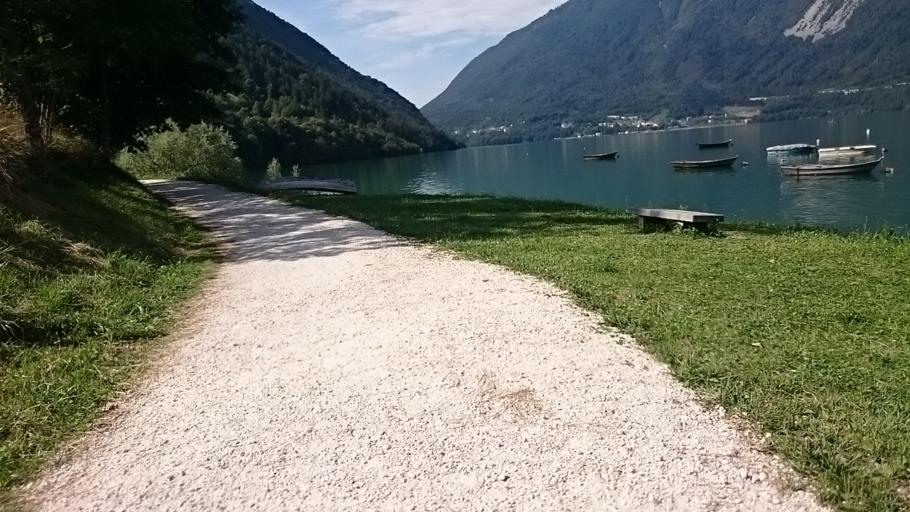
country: IT
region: Veneto
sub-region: Provincia di Belluno
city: Farra d'Alpago
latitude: 46.1075
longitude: 12.3528
